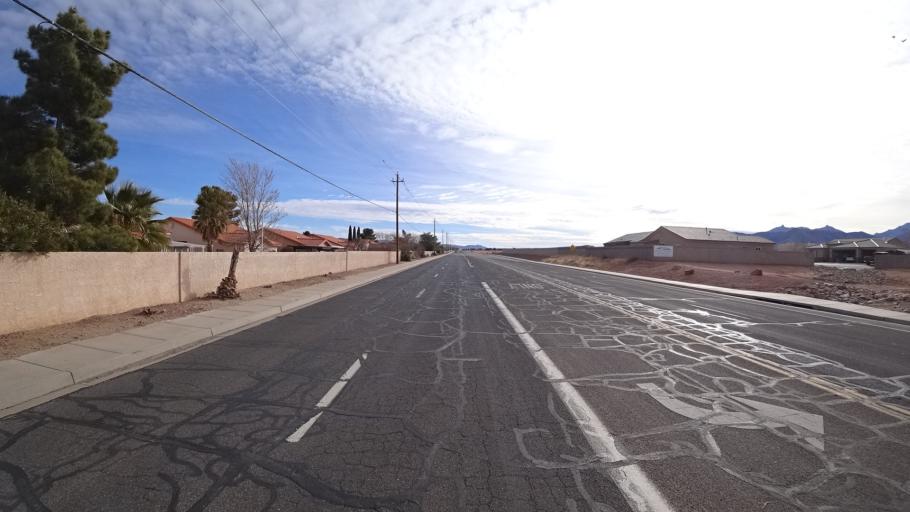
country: US
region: Arizona
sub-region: Mohave County
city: New Kingman-Butler
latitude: 35.2249
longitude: -113.9915
